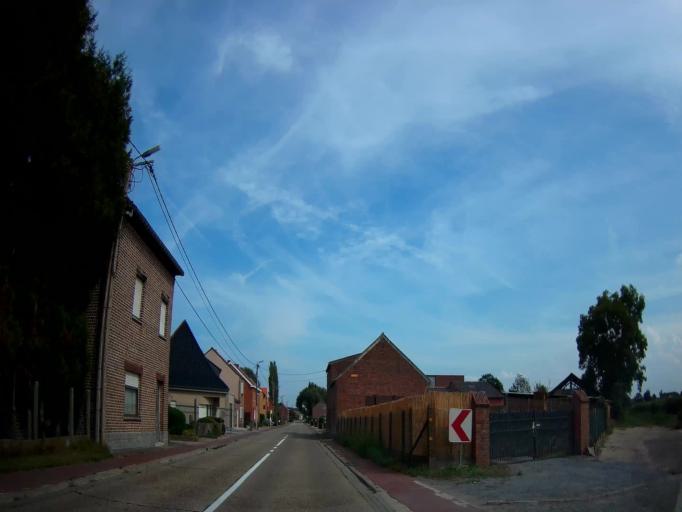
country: BE
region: Flanders
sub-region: Provincie Vlaams-Brabant
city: Zoutleeuw
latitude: 50.8279
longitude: 5.1187
